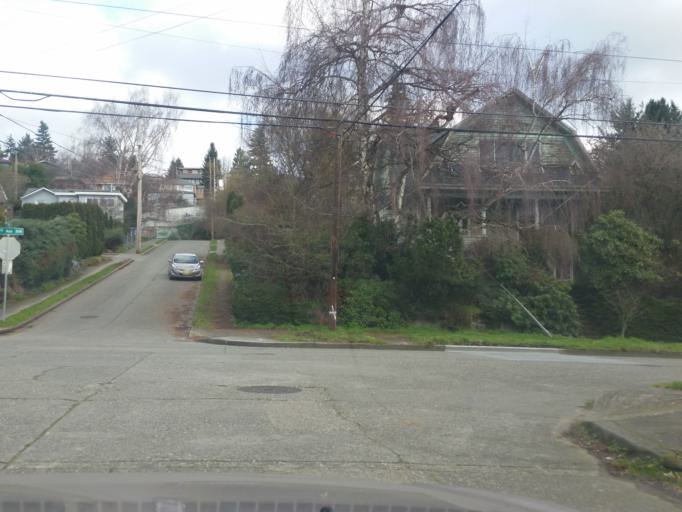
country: US
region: Washington
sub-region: King County
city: Seattle
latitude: 47.6578
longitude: -122.3611
